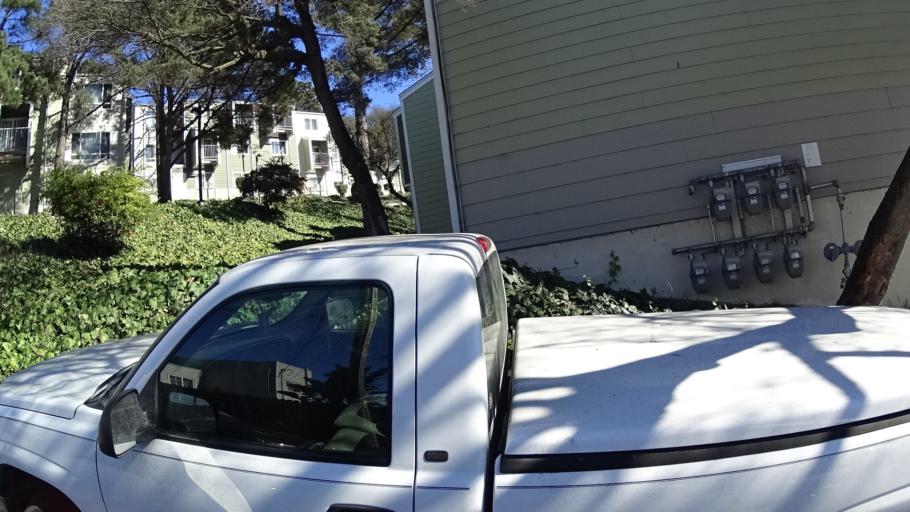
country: US
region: California
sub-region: San Francisco County
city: San Francisco
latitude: 37.7350
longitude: -122.3872
